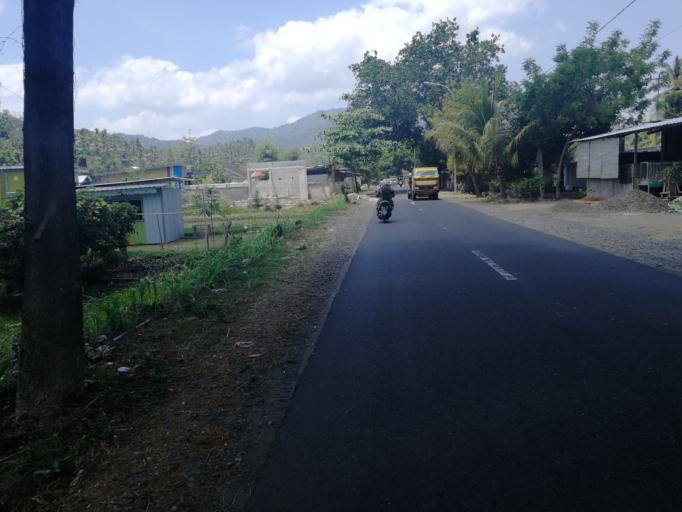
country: ID
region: West Nusa Tenggara
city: Karangsubagan
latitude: -8.4324
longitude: 116.0891
